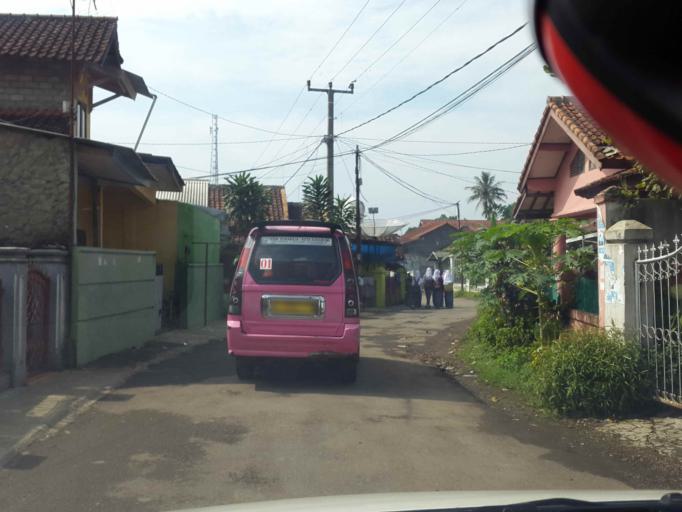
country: ID
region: West Java
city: Sukabumi
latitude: -6.9146
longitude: 106.9717
